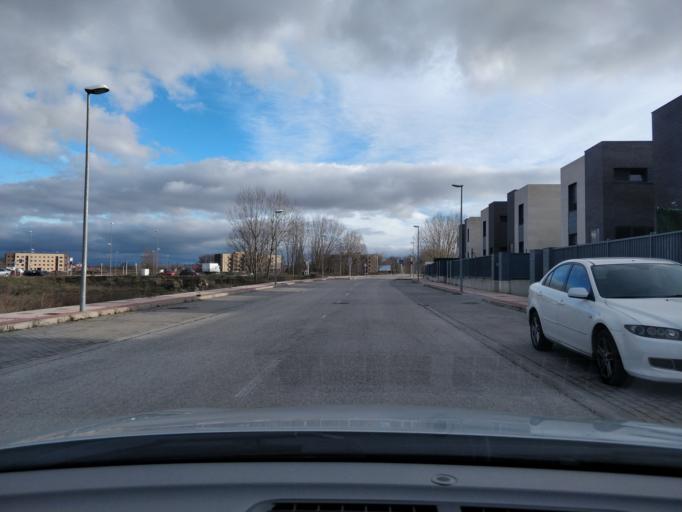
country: ES
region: Castille and Leon
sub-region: Provincia de Burgos
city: Villalbilla de Burgos
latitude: 42.3553
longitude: -3.7615
